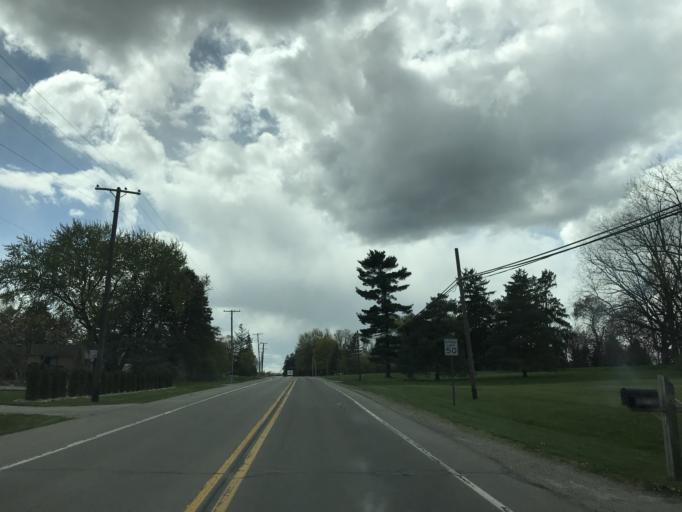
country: US
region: Michigan
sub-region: Wayne County
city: Plymouth
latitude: 42.3778
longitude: -83.5028
